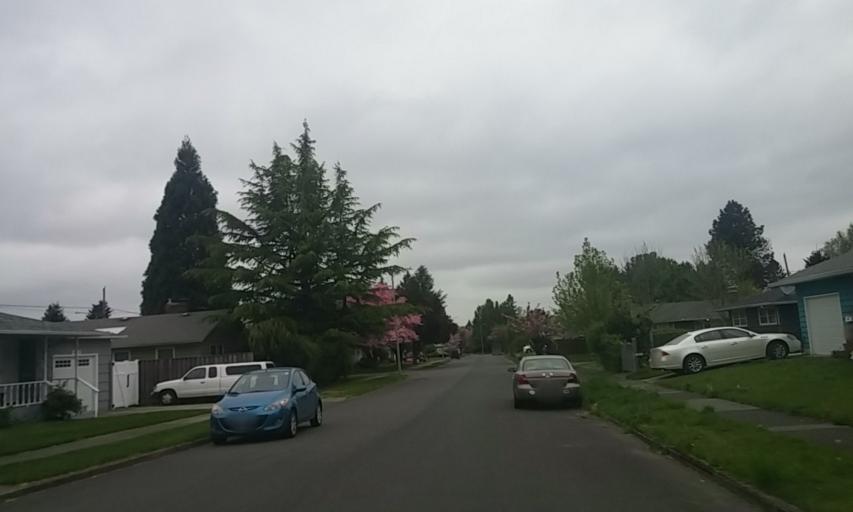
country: US
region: Oregon
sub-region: Multnomah County
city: Lents
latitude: 45.5054
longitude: -122.5573
